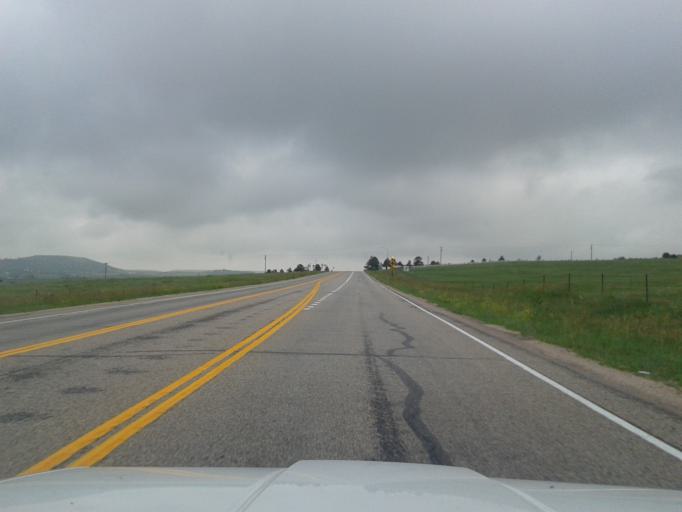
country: US
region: Colorado
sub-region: El Paso County
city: Woodmoor
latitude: 39.1266
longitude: -104.7665
